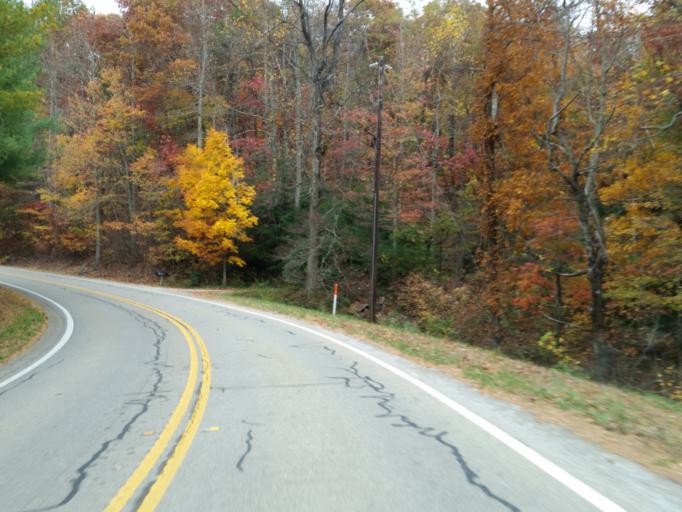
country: US
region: Georgia
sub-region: Pickens County
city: Jasper
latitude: 34.5424
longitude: -84.3657
